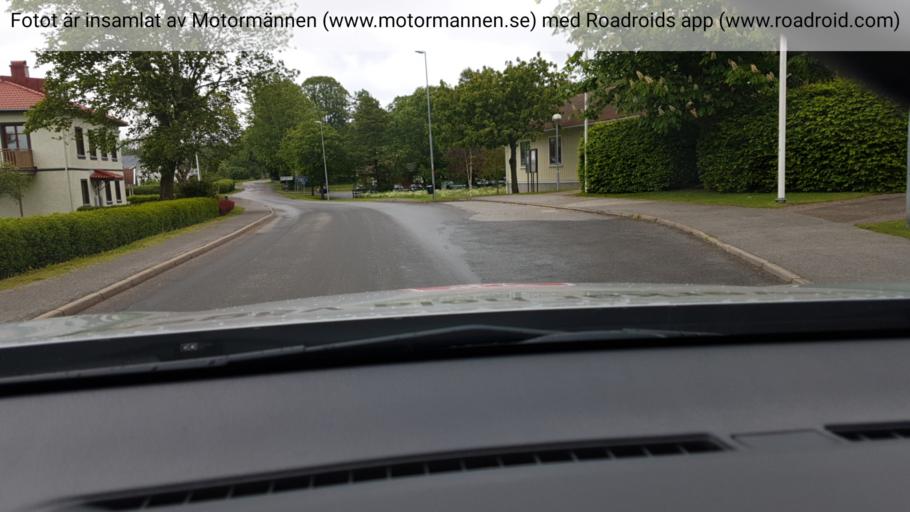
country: SE
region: Vaestra Goetaland
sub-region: Skara Kommun
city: Axvall
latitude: 58.3862
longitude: 13.6513
